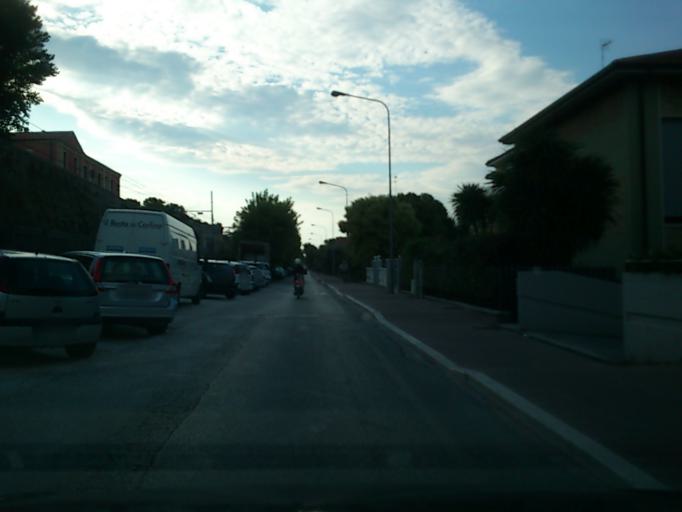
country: IT
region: The Marches
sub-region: Provincia di Pesaro e Urbino
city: Fano
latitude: 43.8462
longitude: 13.0181
